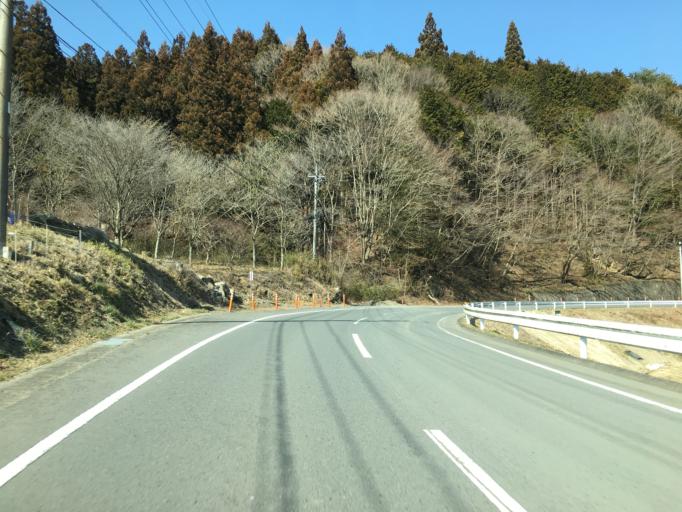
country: JP
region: Ibaraki
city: Daigo
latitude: 36.8168
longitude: 140.5150
